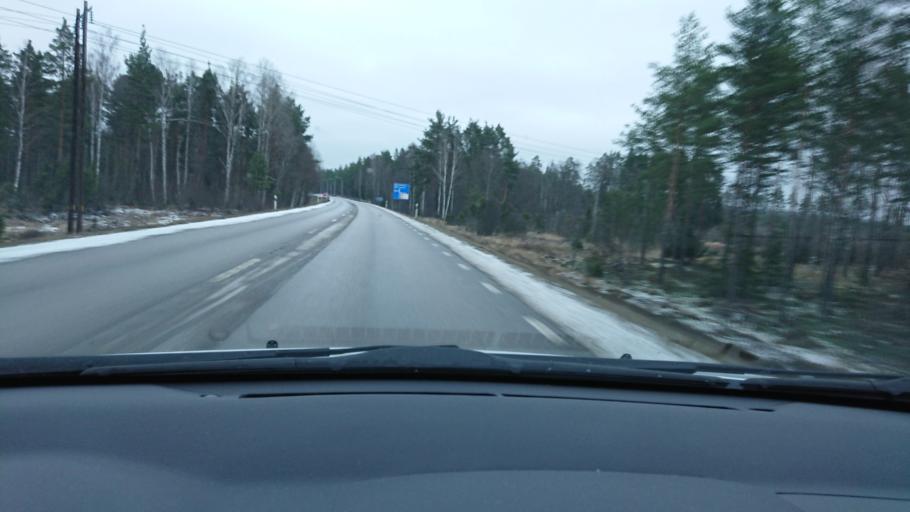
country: SE
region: Kalmar
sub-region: Hultsfreds Kommun
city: Hultsfred
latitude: 57.5132
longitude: 15.8393
